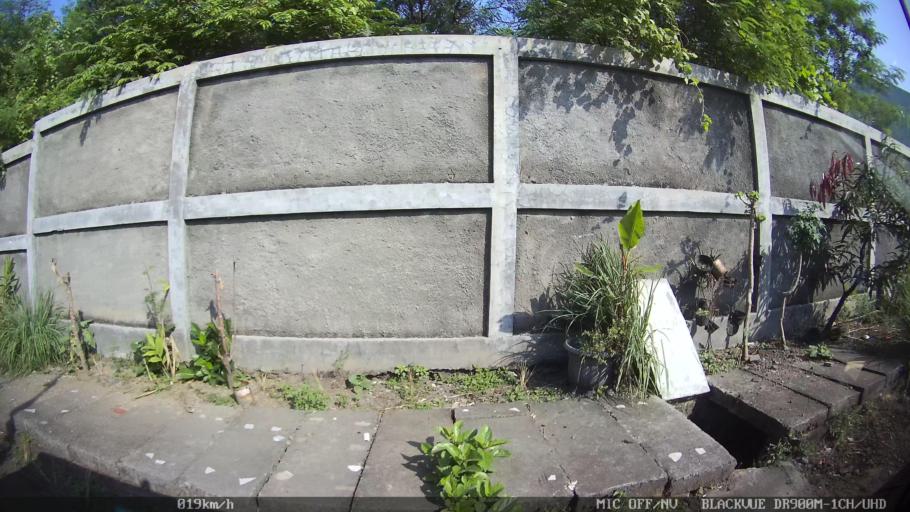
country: ID
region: Daerah Istimewa Yogyakarta
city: Depok
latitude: -7.7592
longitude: 110.4005
